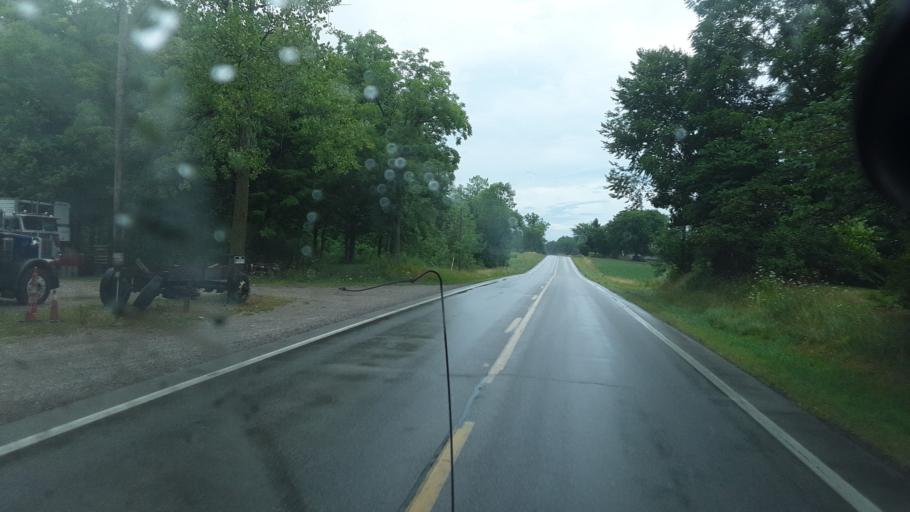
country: US
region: Indiana
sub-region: Steuben County
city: Hamilton
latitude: 41.6325
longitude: -84.7947
